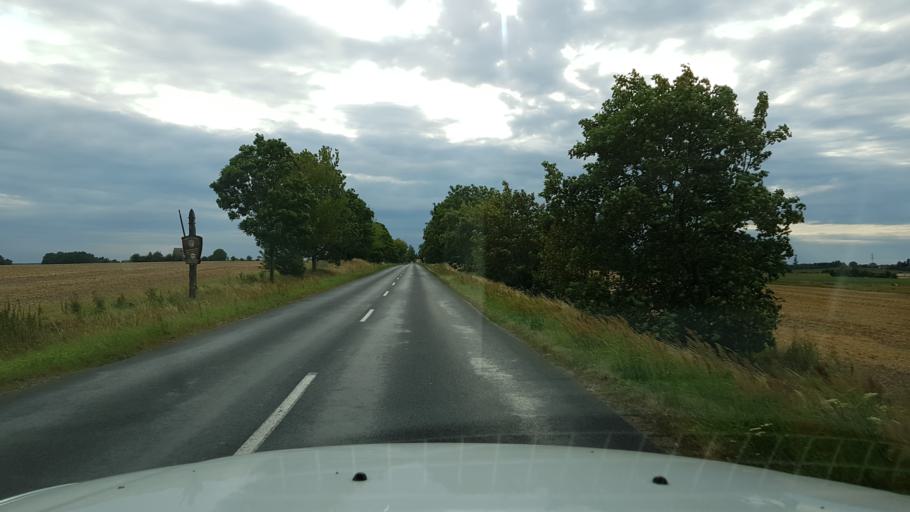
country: PL
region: West Pomeranian Voivodeship
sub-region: Powiat kolobrzeski
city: Dygowo
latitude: 54.1464
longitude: 15.6550
